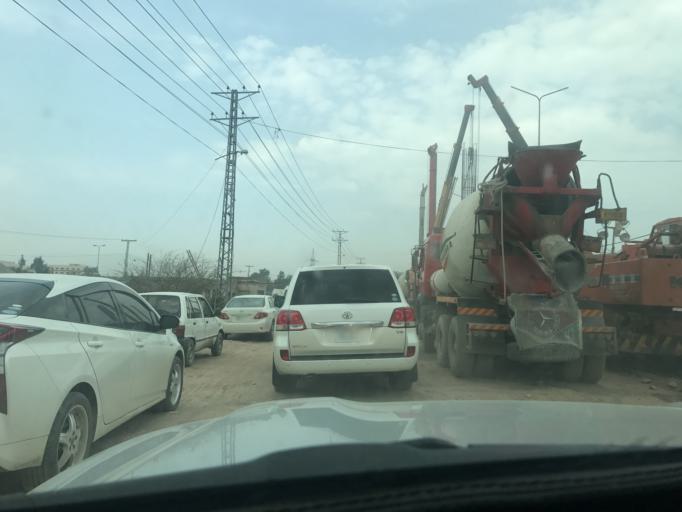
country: PK
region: Khyber Pakhtunkhwa
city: Peshawar
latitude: 33.9973
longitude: 71.4386
